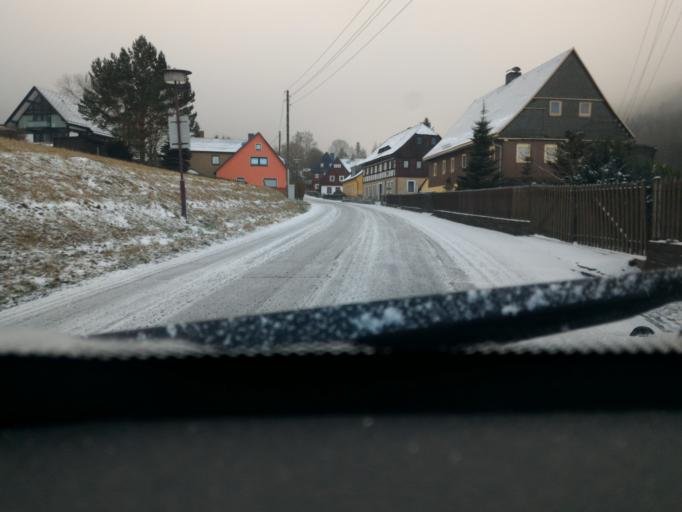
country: DE
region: Saxony
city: Grossschonau
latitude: 50.8605
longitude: 14.6528
